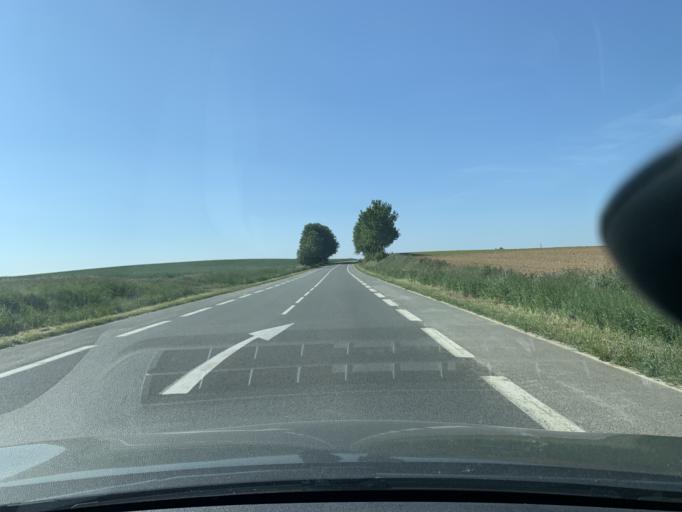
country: FR
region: Nord-Pas-de-Calais
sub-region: Departement du Nord
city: Rumilly-en-Cambresis
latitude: 50.1268
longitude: 3.2461
